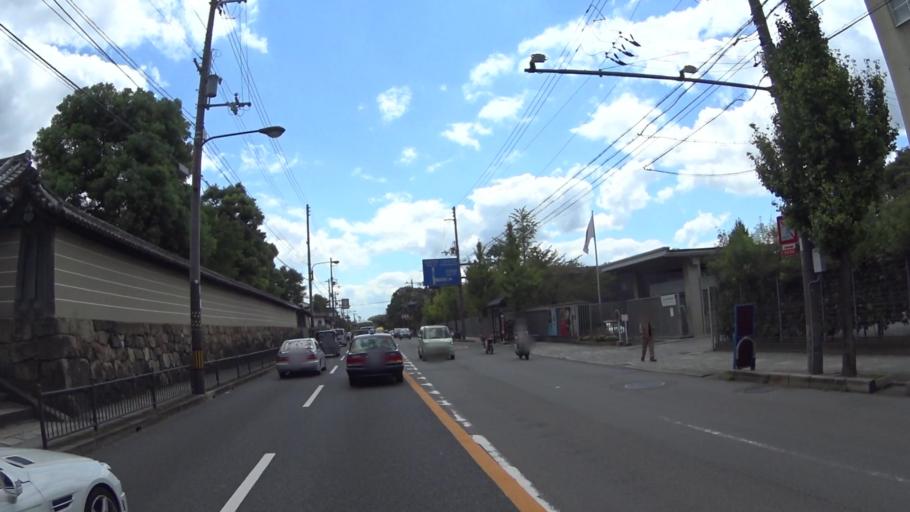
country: JP
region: Kyoto
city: Kyoto
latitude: 34.9906
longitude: 135.7746
